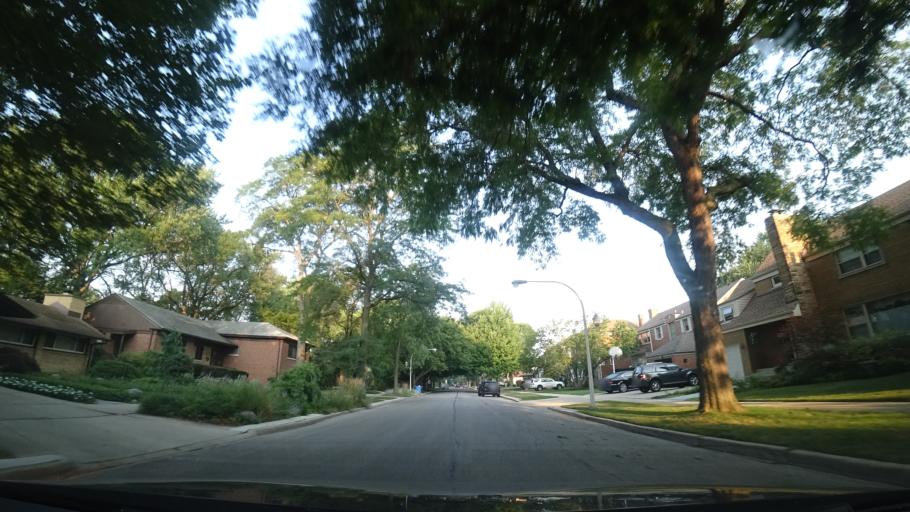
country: US
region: Illinois
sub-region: Cook County
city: Lincolnwood
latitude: 41.9812
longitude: -87.7023
